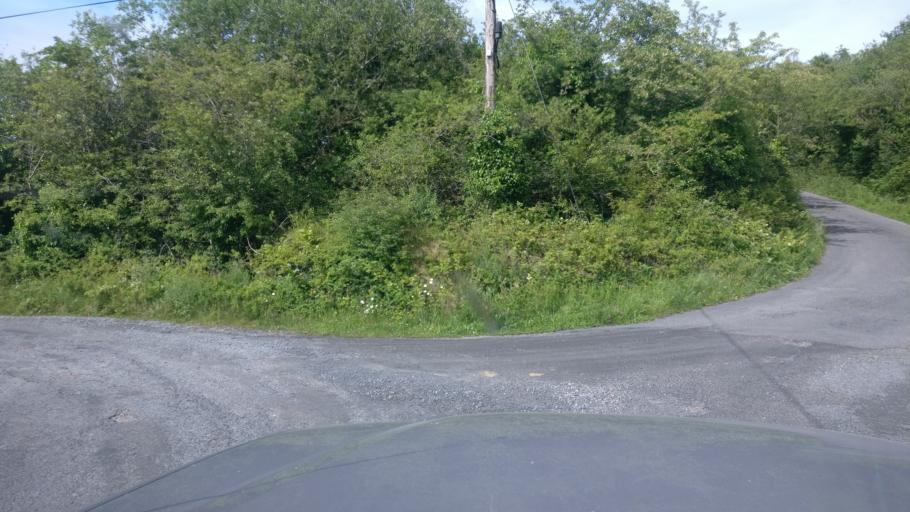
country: IE
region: Connaught
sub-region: County Galway
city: Gort
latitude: 53.0972
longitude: -8.6964
